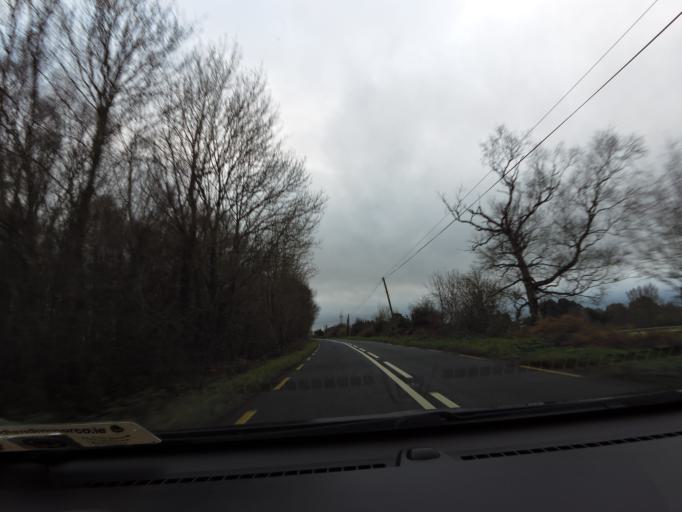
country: IE
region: Connaught
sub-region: County Galway
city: Portumna
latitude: 53.1441
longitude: -8.2567
